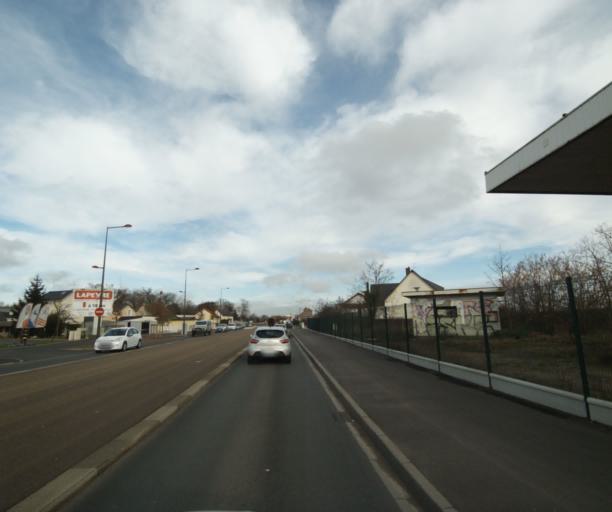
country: FR
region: Pays de la Loire
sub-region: Departement de la Sarthe
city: Allonnes
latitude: 47.9840
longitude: 0.1777
